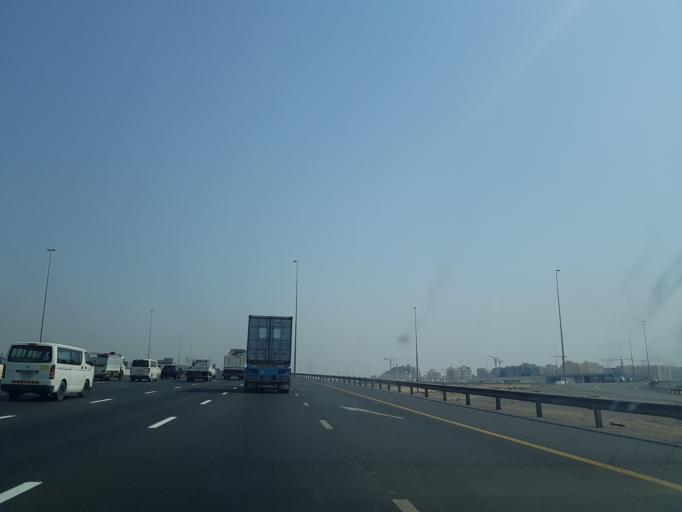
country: AE
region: Ash Shariqah
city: Sharjah
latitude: 25.1757
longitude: 55.3965
